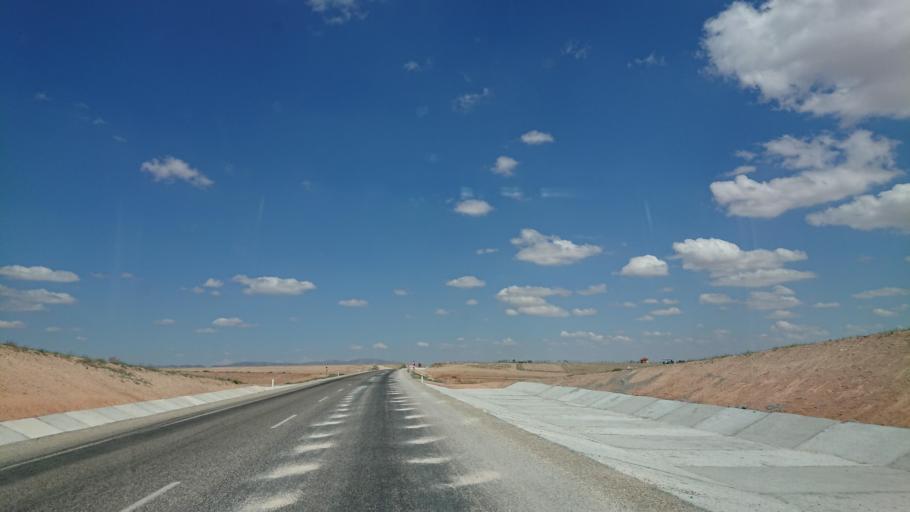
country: TR
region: Kirsehir
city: Kirsehir
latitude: 39.1242
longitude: 33.9886
